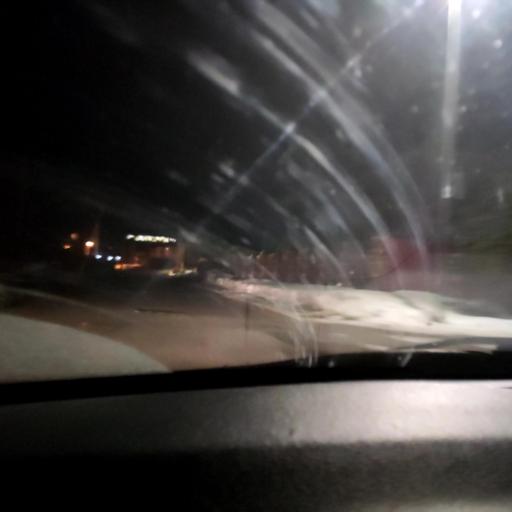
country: RU
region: Bashkortostan
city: Avdon
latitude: 54.4888
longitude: 55.8738
